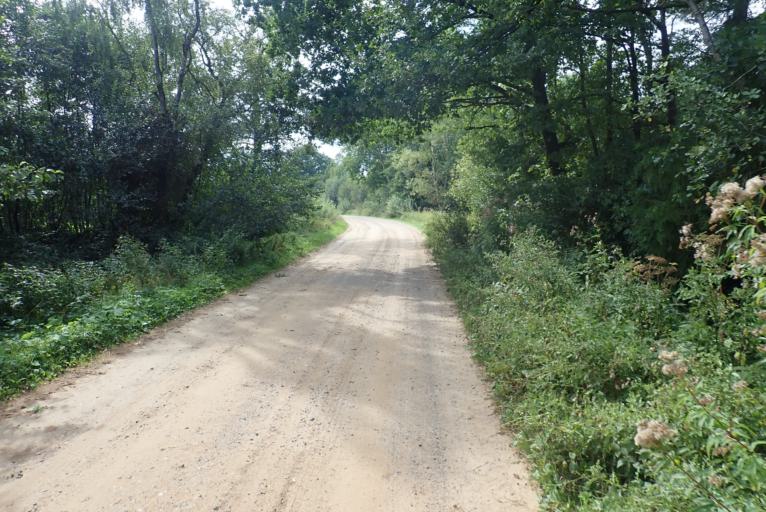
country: BE
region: Flanders
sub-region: Provincie Antwerpen
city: Lille
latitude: 51.2460
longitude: 4.7937
